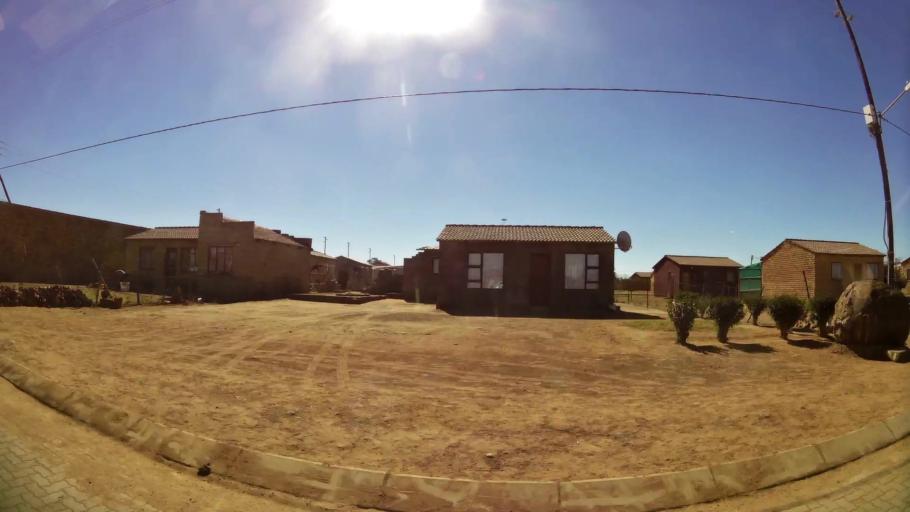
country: ZA
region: North-West
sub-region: Dr Kenneth Kaunda District Municipality
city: Klerksdorp
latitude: -26.8683
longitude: 26.5683
